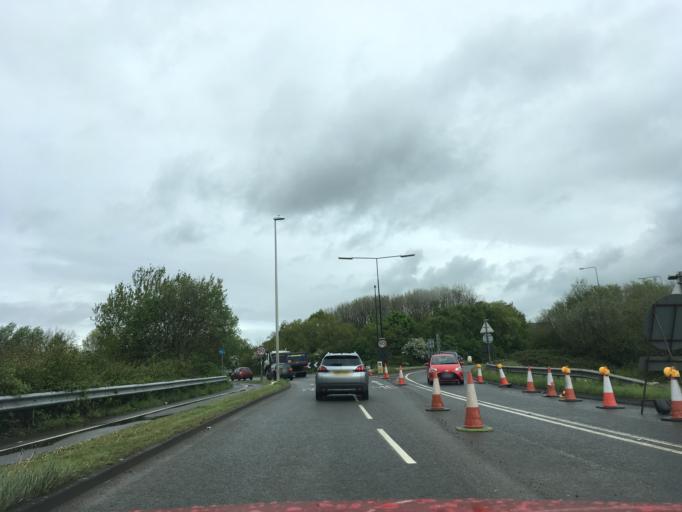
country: GB
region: England
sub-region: North Somerset
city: Hutton
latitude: 51.3437
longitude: -2.9318
